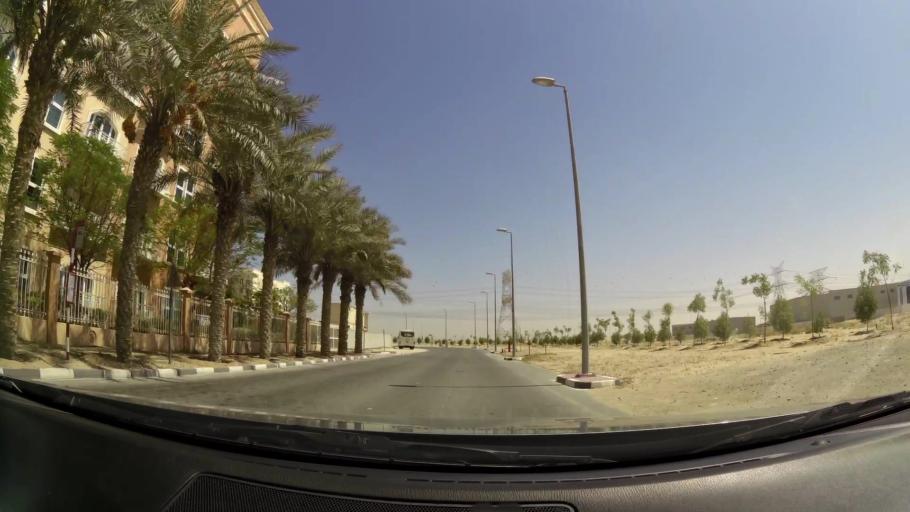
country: AE
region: Dubai
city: Dubai
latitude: 24.9886
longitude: 55.2042
